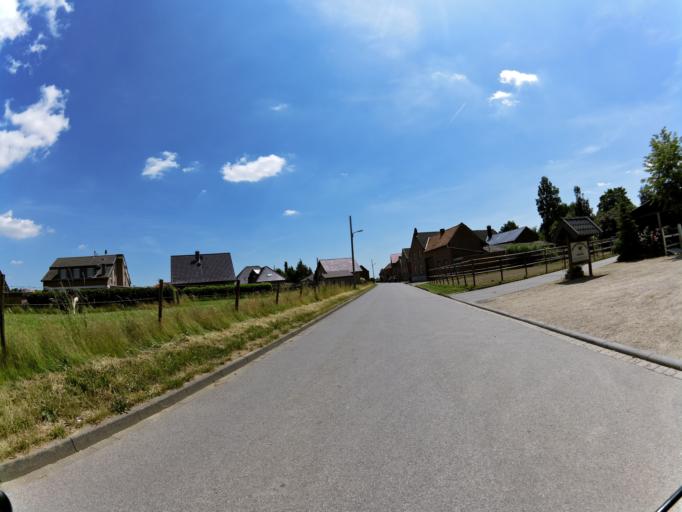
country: DE
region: North Rhine-Westphalia
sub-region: Regierungsbezirk Koln
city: Heinsberg
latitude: 51.0236
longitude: 6.0644
